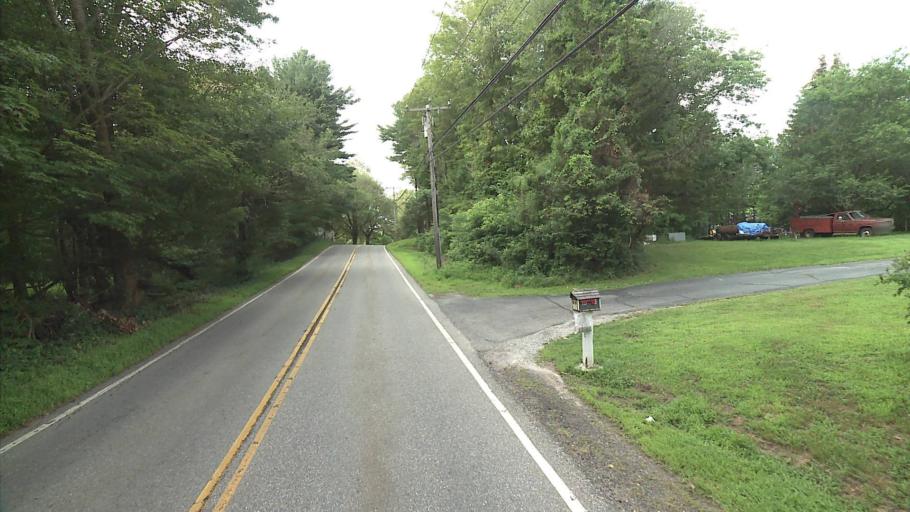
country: US
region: Connecticut
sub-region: Middlesex County
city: Moodus
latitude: 41.5585
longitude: -72.4069
